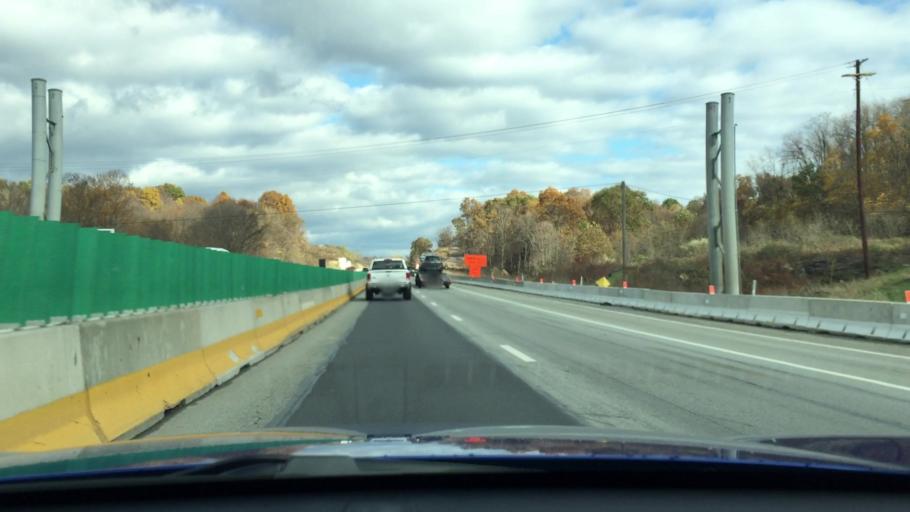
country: US
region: Pennsylvania
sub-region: Westmoreland County
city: West Newton
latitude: 40.1894
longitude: -79.6976
